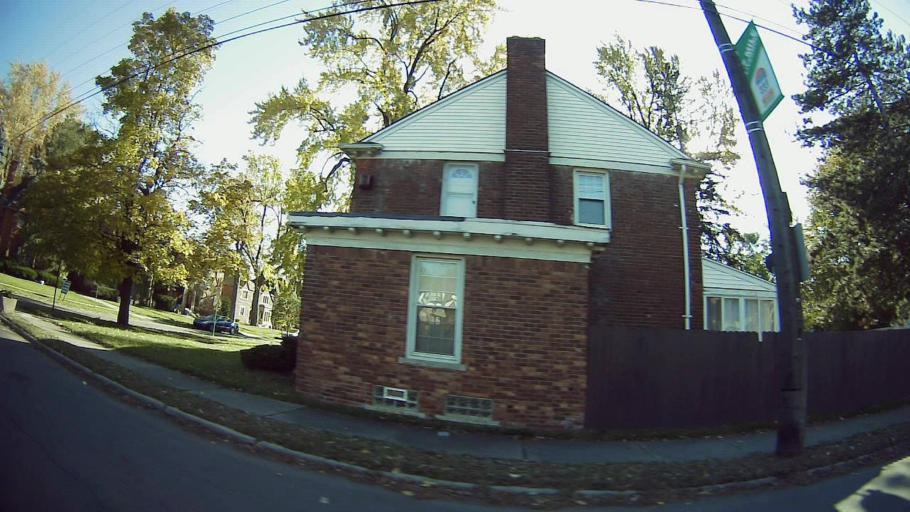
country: US
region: Michigan
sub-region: Oakland County
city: Ferndale
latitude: 42.4317
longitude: -83.1338
